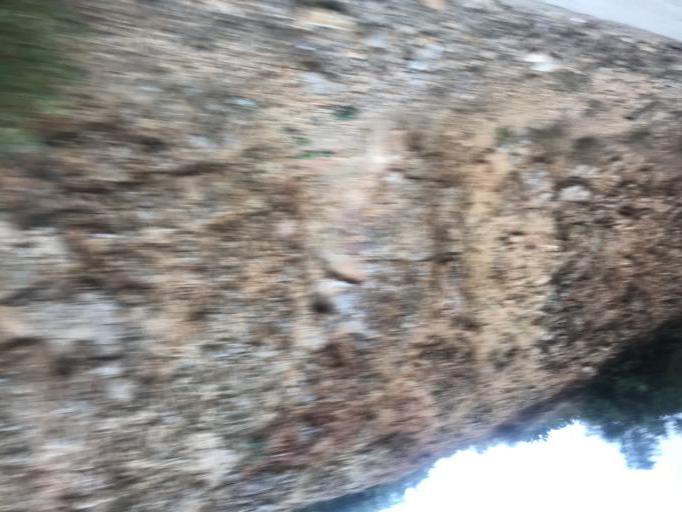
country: TR
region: Balikesir
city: Ergama
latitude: 39.6269
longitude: 27.6100
